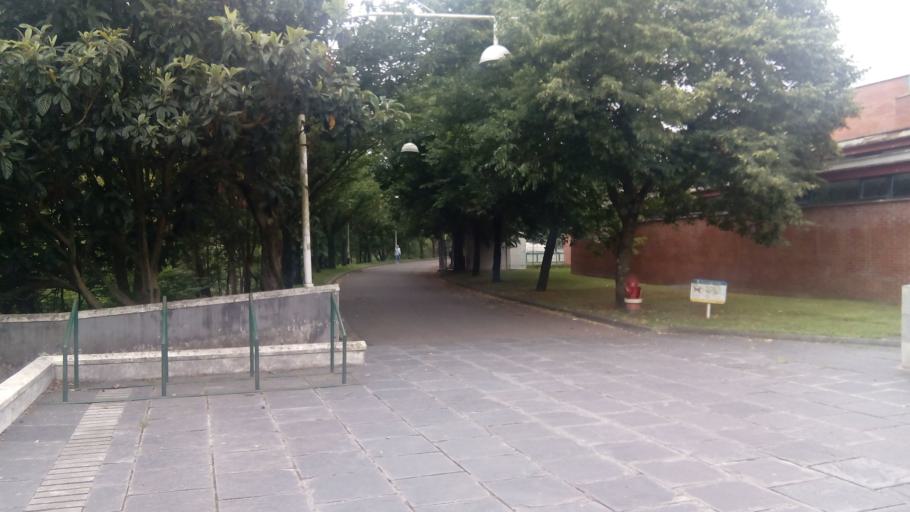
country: ES
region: Basque Country
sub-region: Provincia de Guipuzcoa
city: Andoain
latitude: 43.2150
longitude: -2.0230
